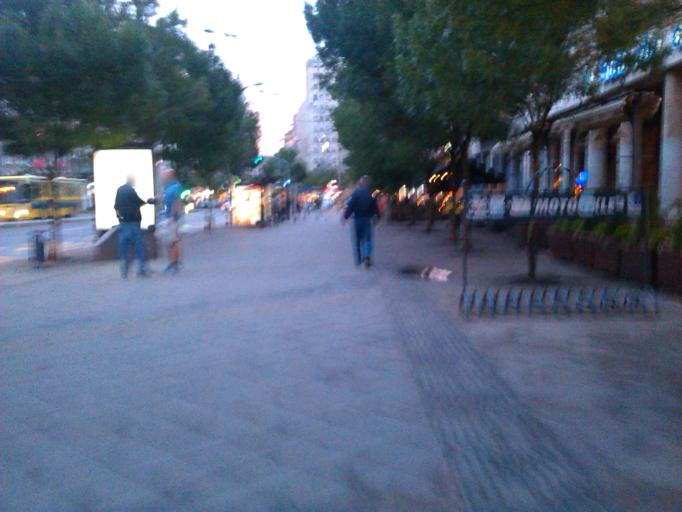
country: RS
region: Central Serbia
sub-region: Belgrade
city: Stari Grad
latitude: 44.8128
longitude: 20.4614
